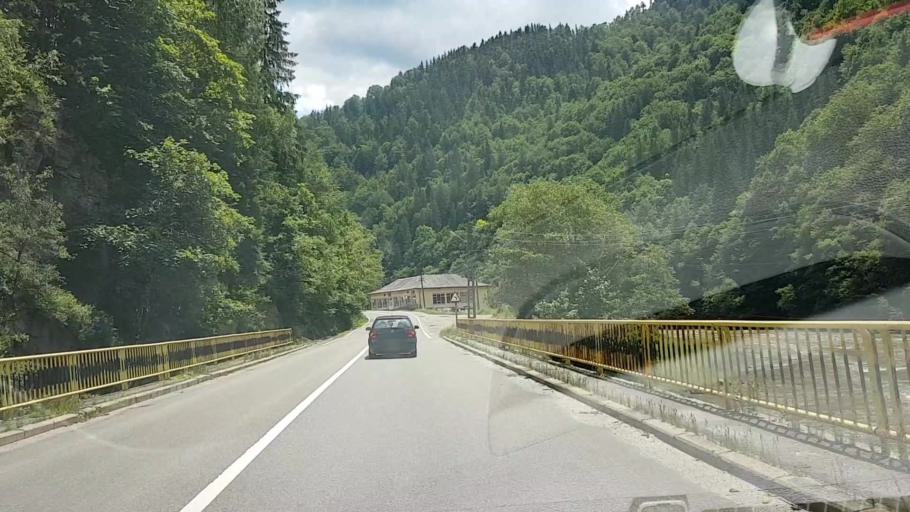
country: RO
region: Suceava
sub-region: Comuna Crucea
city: Crucea
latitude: 47.2851
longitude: 25.6361
